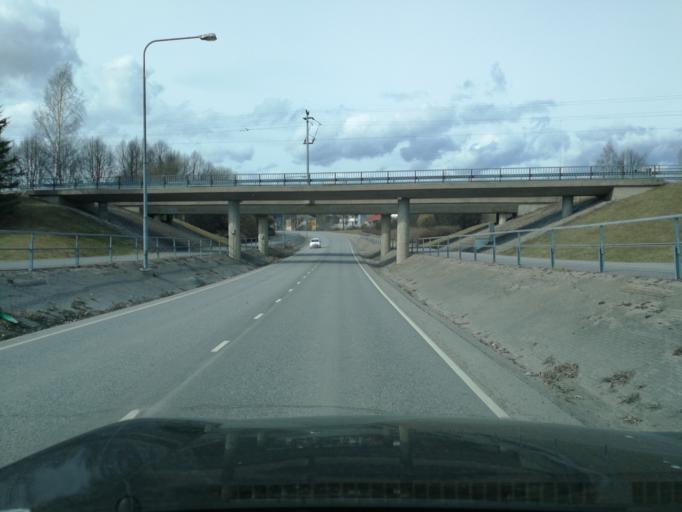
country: FI
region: Uusimaa
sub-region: Helsinki
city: Siuntio
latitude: 60.1404
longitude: 24.2258
